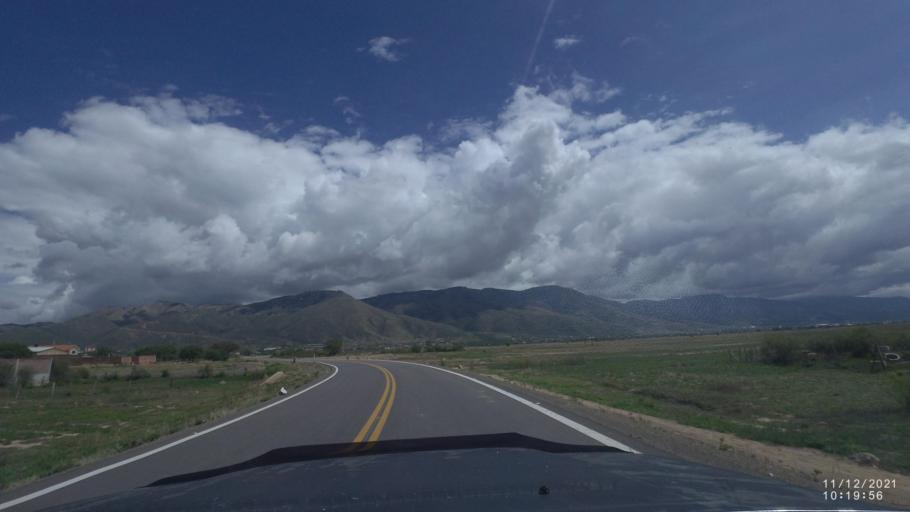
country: BO
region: Cochabamba
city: Tarata
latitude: -17.5632
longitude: -66.0077
